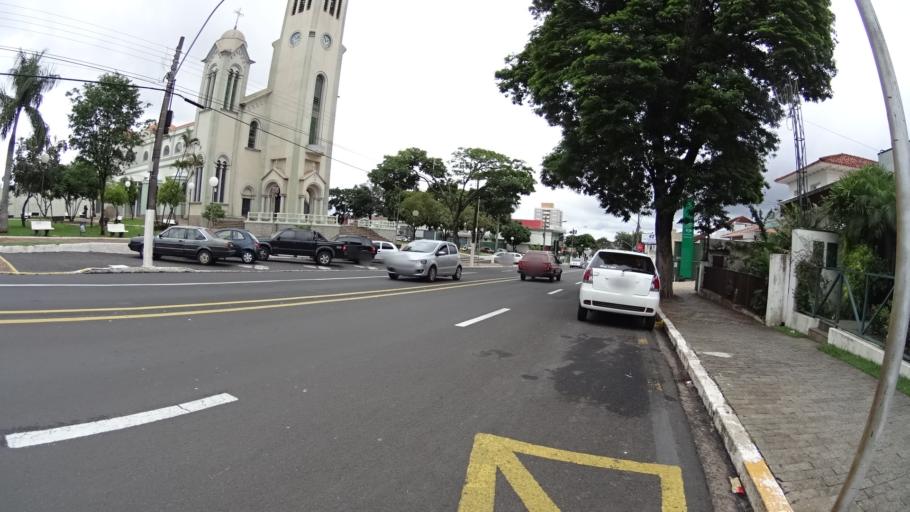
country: BR
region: Sao Paulo
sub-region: Marilia
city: Marilia
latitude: -22.2188
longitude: -49.9530
